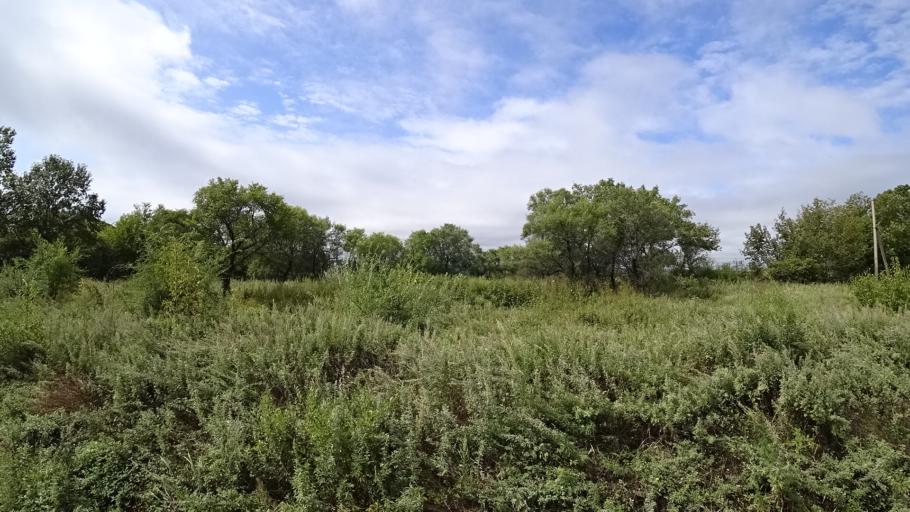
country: RU
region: Primorskiy
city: Lyalichi
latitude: 44.1390
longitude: 132.3749
